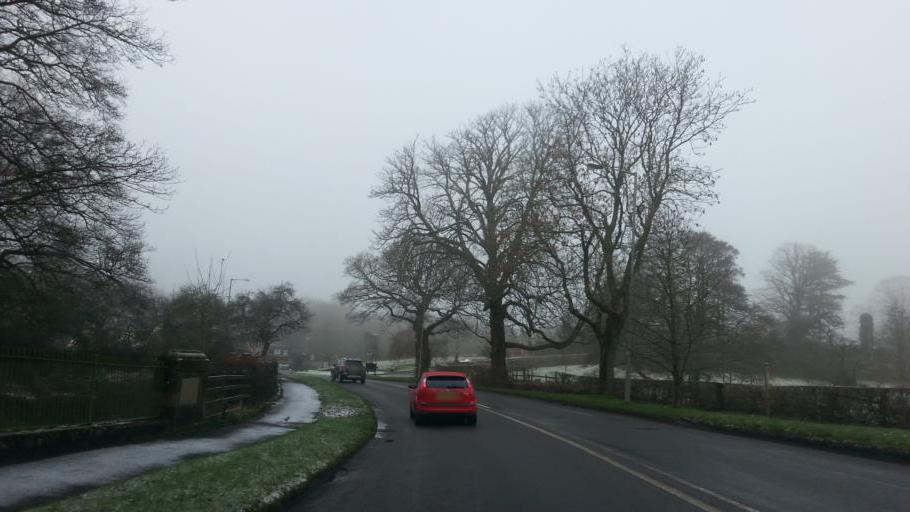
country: GB
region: England
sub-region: Staffordshire
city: Biddulph
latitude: 53.1329
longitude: -2.1662
